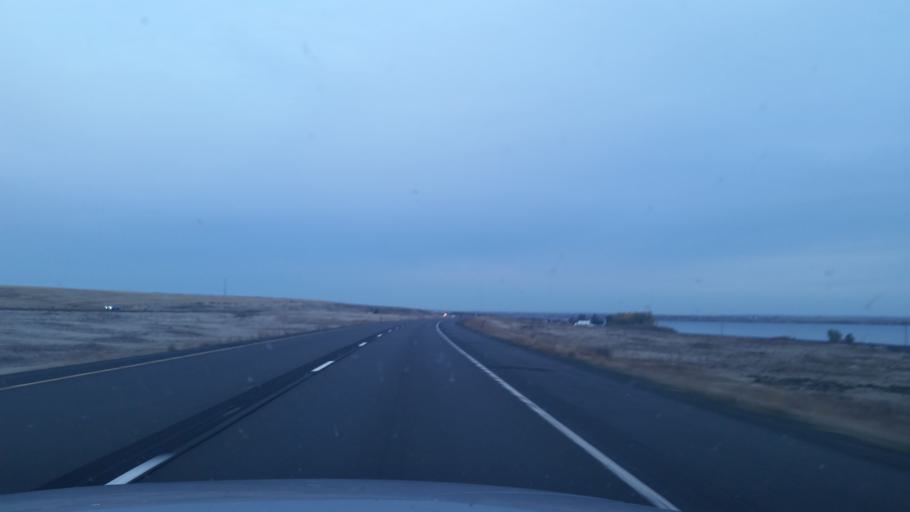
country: US
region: Washington
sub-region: Adams County
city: Ritzville
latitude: 47.2519
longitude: -118.0999
